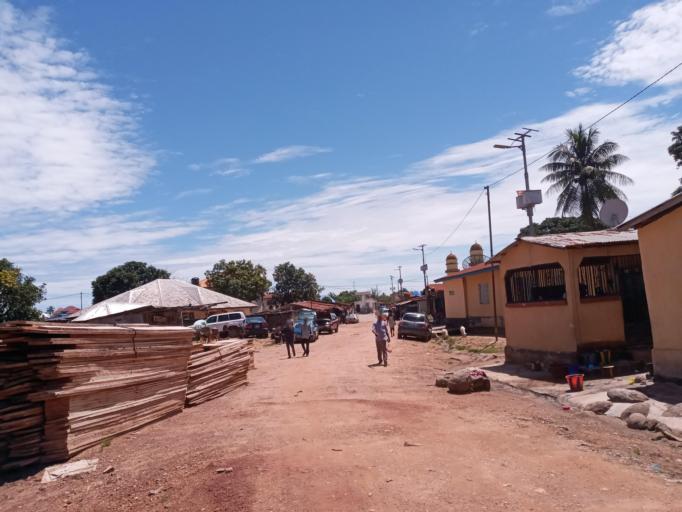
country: SL
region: Eastern Province
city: Koidu
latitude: 8.6408
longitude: -10.9730
